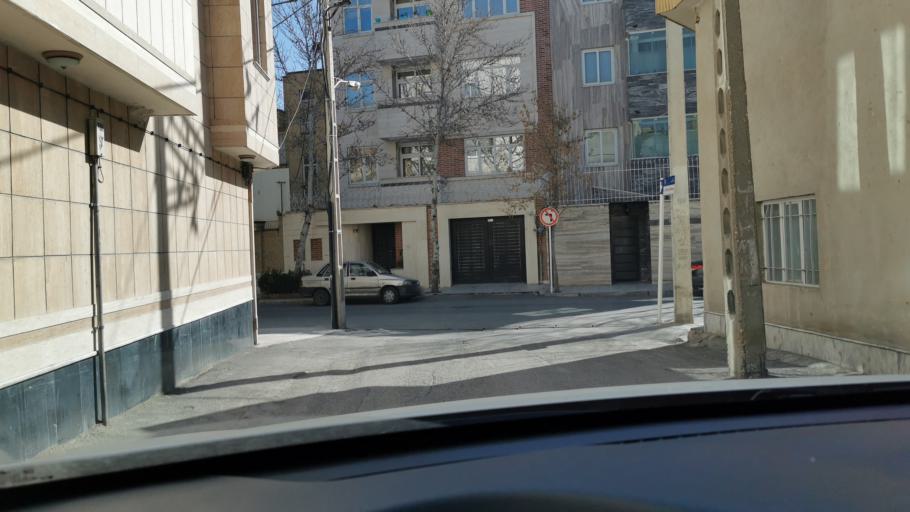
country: IR
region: Razavi Khorasan
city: Mashhad
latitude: 36.2901
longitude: 59.5784
